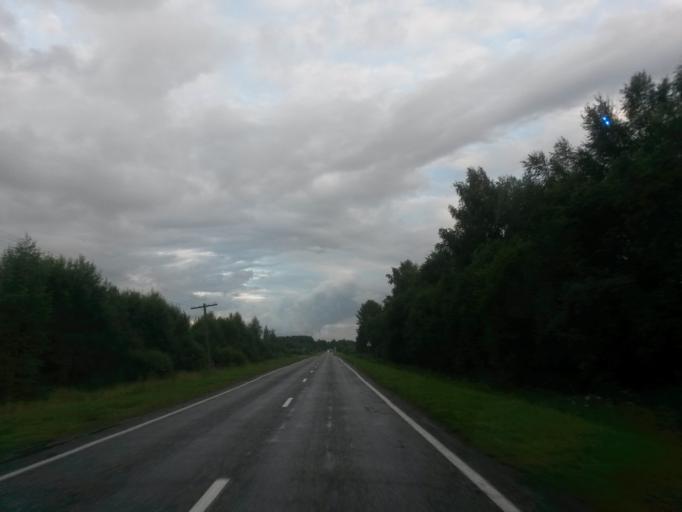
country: RU
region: Jaroslavl
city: Tutayev
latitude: 57.9074
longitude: 39.5204
